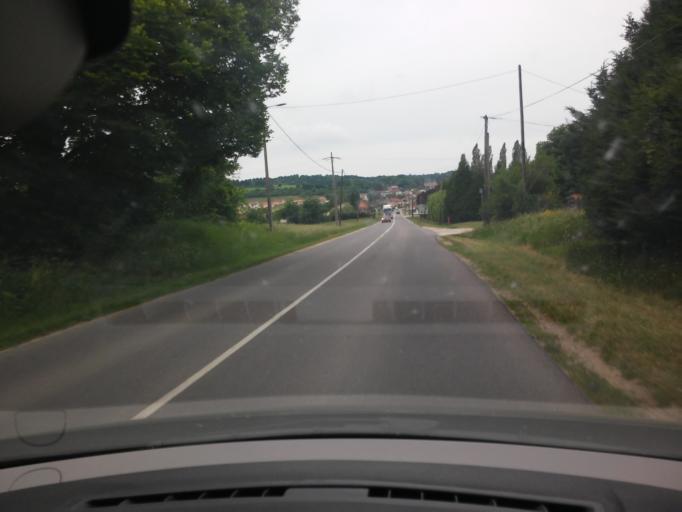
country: FR
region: Lorraine
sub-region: Departement de la Meuse
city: Lerouville
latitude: 48.8181
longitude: 5.5146
